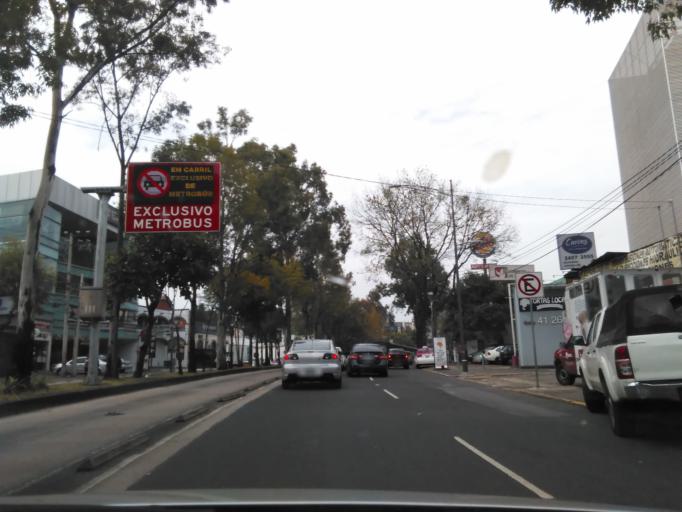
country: MX
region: Mexico City
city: Tlalpan
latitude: 19.2823
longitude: -99.1743
